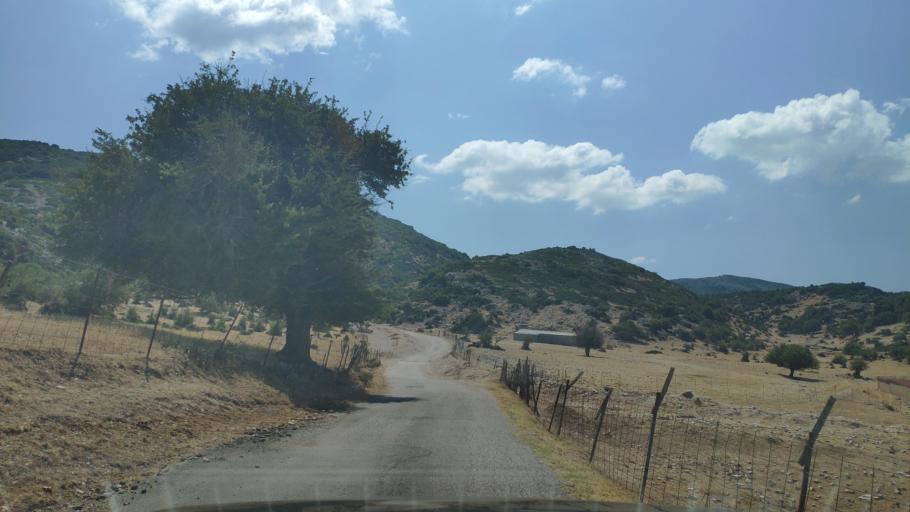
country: GR
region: West Greece
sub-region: Nomos Aitolias kai Akarnanias
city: Monastirakion
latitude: 38.8076
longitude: 20.9424
